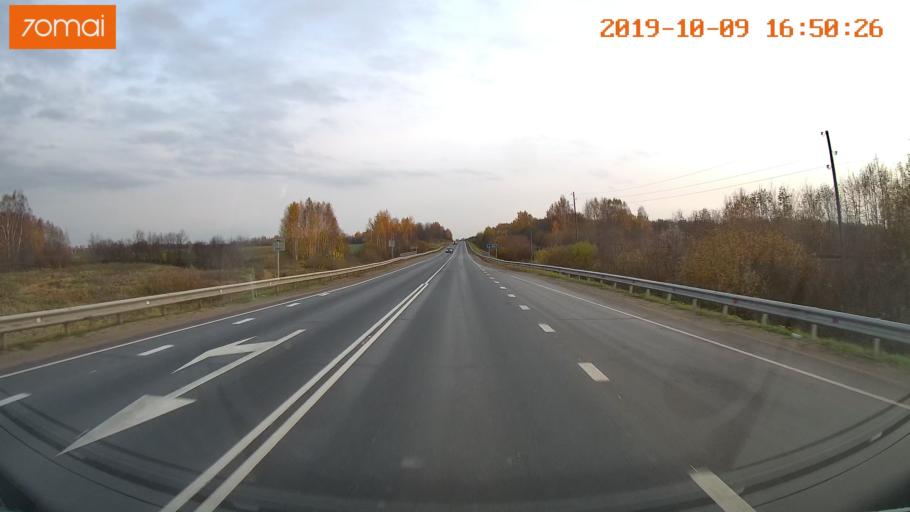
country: RU
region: Kostroma
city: Volgorechensk
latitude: 57.4008
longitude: 41.2090
